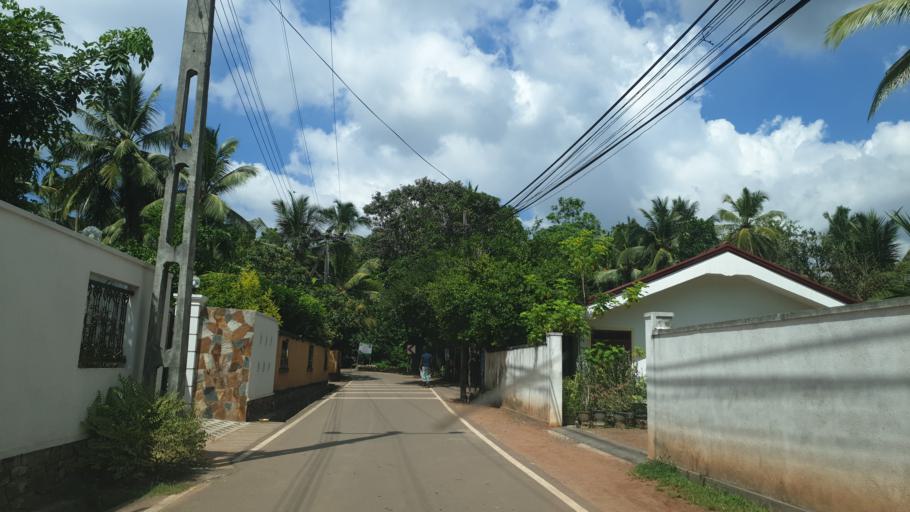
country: LK
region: Western
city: Panadura
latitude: 6.6766
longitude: 79.9712
